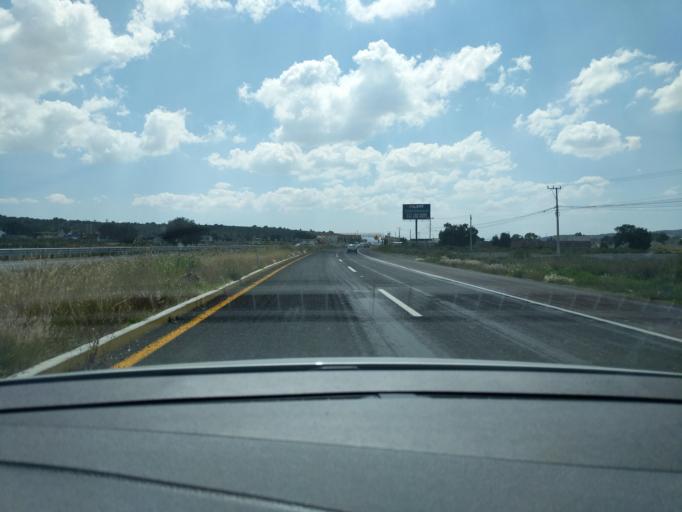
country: MX
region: Hidalgo
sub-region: Mineral de la Reforma
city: Rinconada de los Angeles
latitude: 19.9937
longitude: -98.7072
